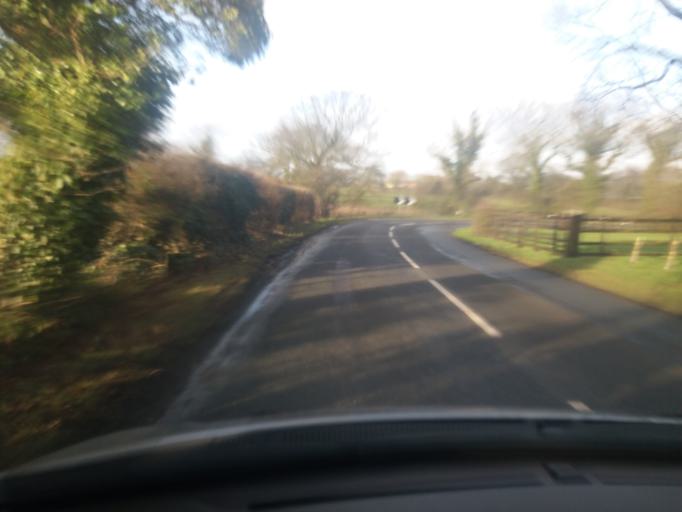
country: GB
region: England
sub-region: Lancashire
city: Euxton
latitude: 53.6655
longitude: -2.7149
